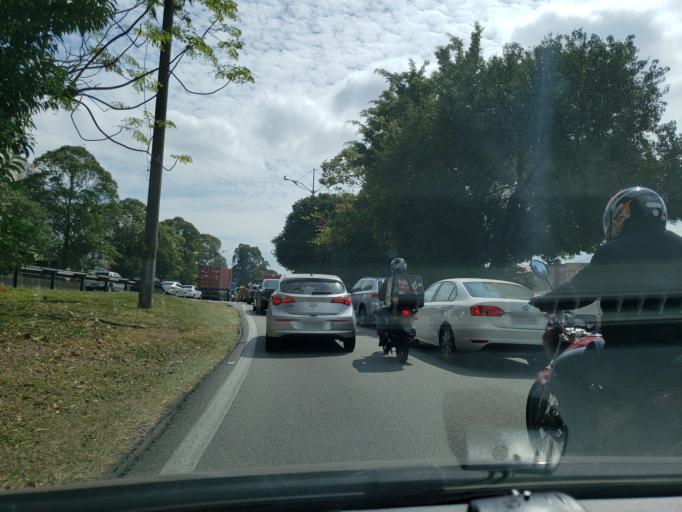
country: BR
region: Sao Paulo
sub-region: Sao Caetano Do Sul
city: Sao Caetano do Sul
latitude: -23.6259
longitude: -46.5985
